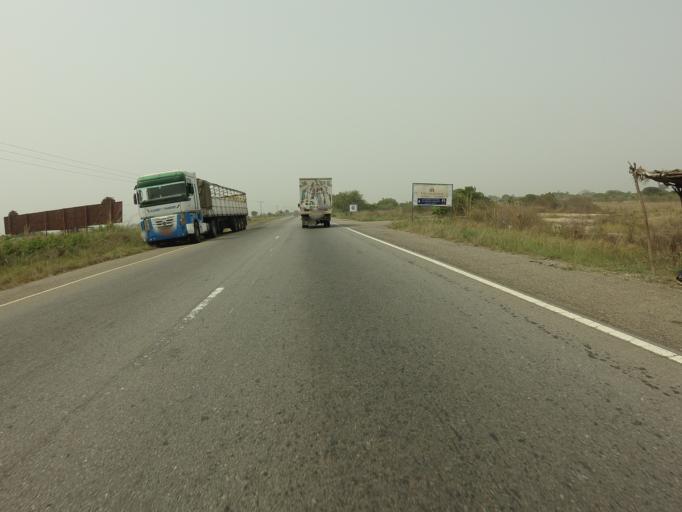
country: GH
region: Volta
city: Anloga
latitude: 5.8868
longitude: 0.4495
